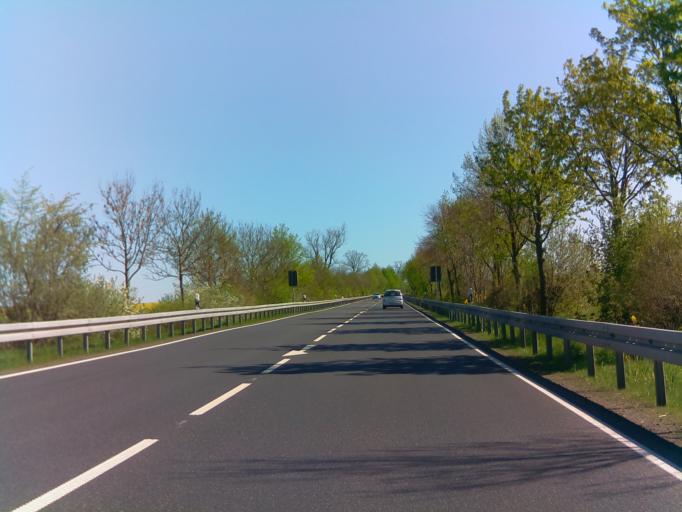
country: DE
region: Hesse
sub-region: Regierungsbezirk Giessen
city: Lauterbach
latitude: 50.6720
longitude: 9.3572
